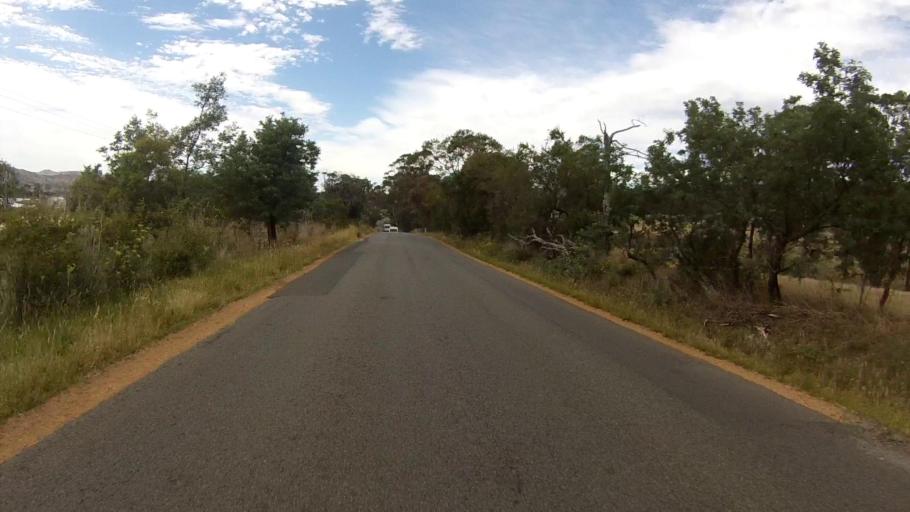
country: AU
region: Tasmania
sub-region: Clarence
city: Lindisfarne
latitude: -42.7523
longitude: 147.3769
